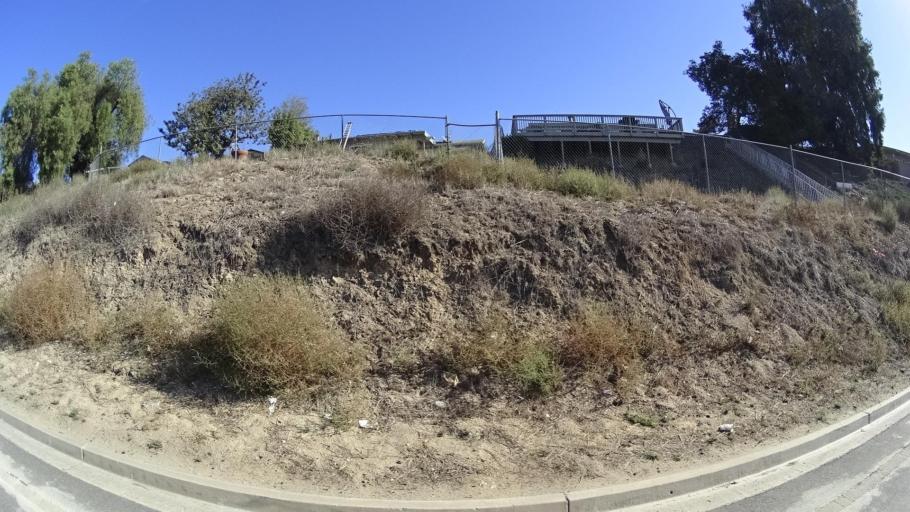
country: US
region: California
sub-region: San Diego County
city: La Presa
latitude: 32.7181
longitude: -117.0213
